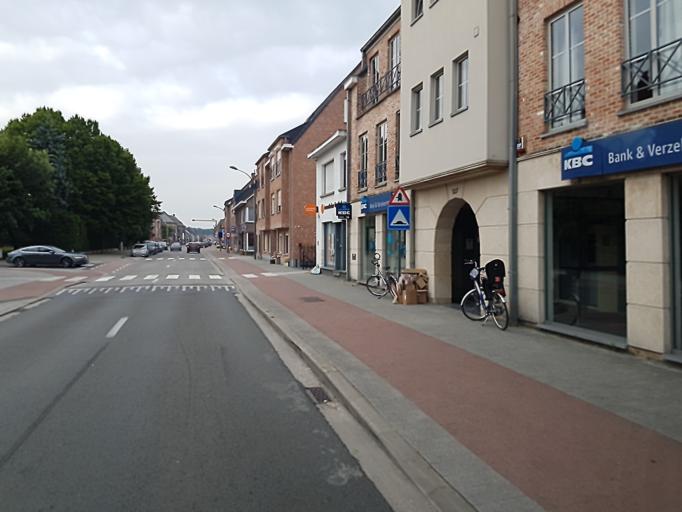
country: BE
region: Flanders
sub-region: Provincie Antwerpen
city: Schilde
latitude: 51.2992
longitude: 4.5723
